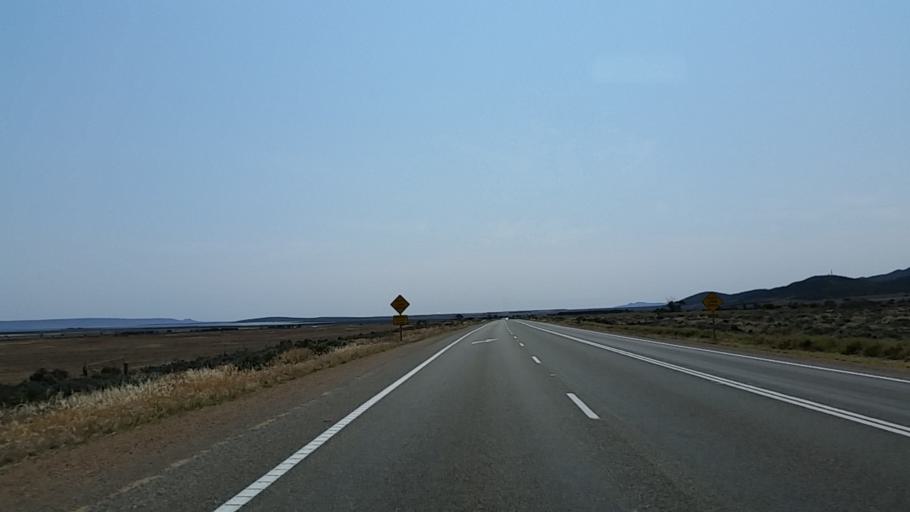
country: AU
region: South Australia
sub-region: Port Augusta
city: Port Augusta
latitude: -32.8000
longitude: 137.9609
